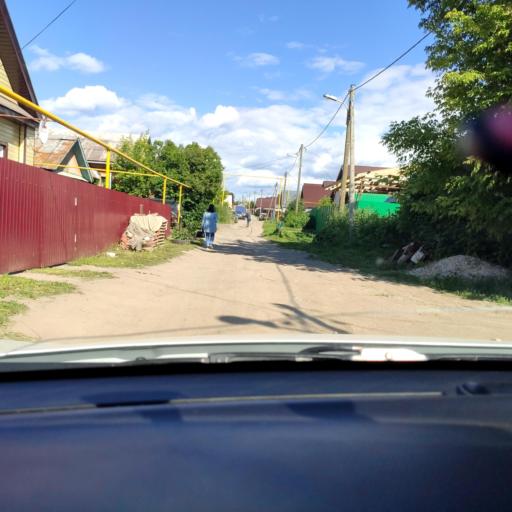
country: RU
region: Tatarstan
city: Vysokaya Gora
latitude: 55.7993
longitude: 49.2669
